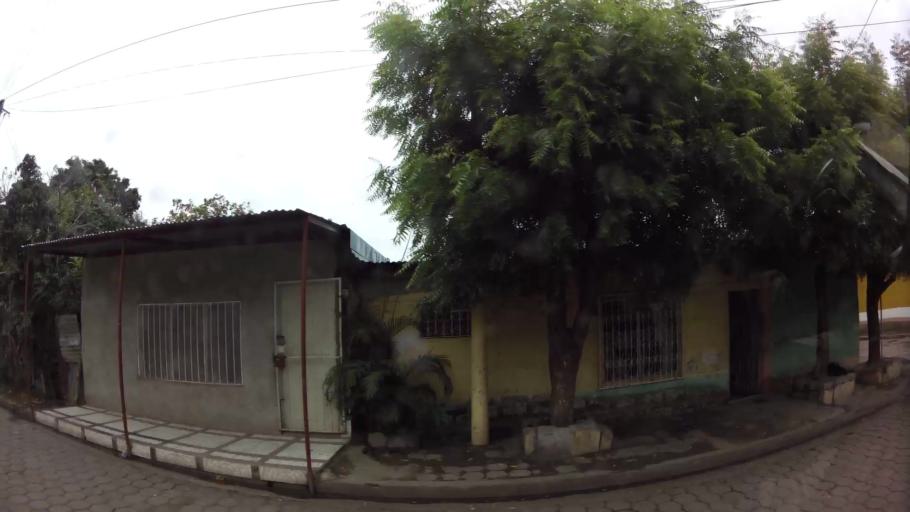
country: NI
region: Granada
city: Nandaime
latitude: 11.7557
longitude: -86.0559
